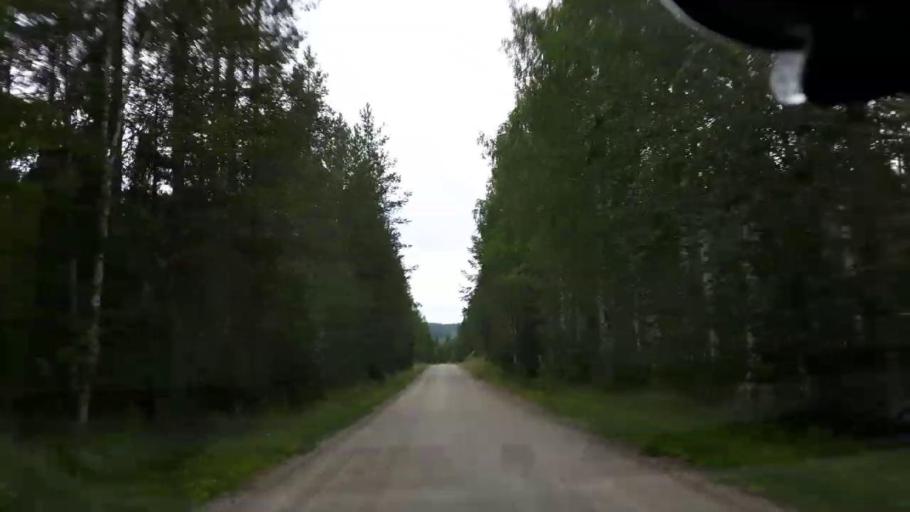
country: SE
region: Vaesternorrland
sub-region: Ange Kommun
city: Ange
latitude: 62.8209
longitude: 15.7152
